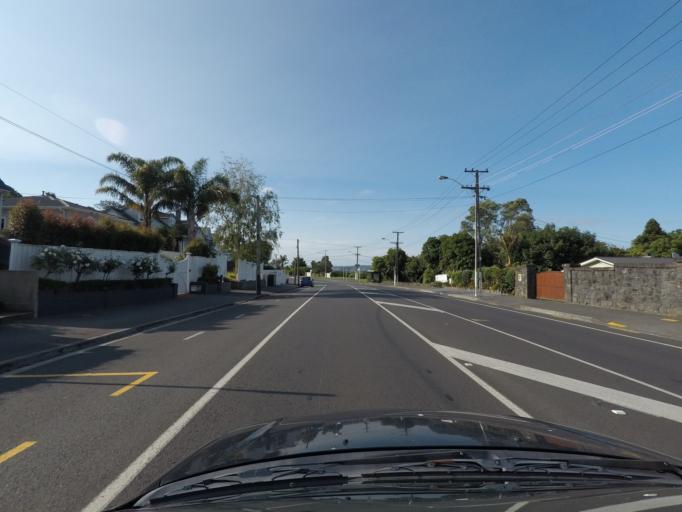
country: NZ
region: Auckland
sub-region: Auckland
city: Auckland
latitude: -36.8907
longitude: 174.7244
